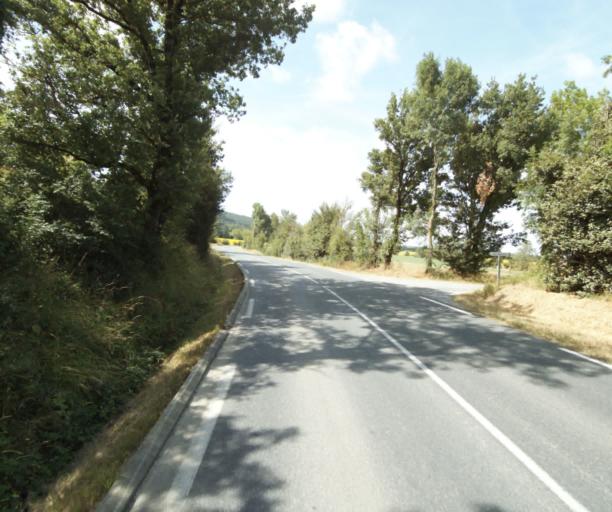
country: FR
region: Midi-Pyrenees
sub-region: Departement du Tarn
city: Dourgne
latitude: 43.4730
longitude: 2.1050
